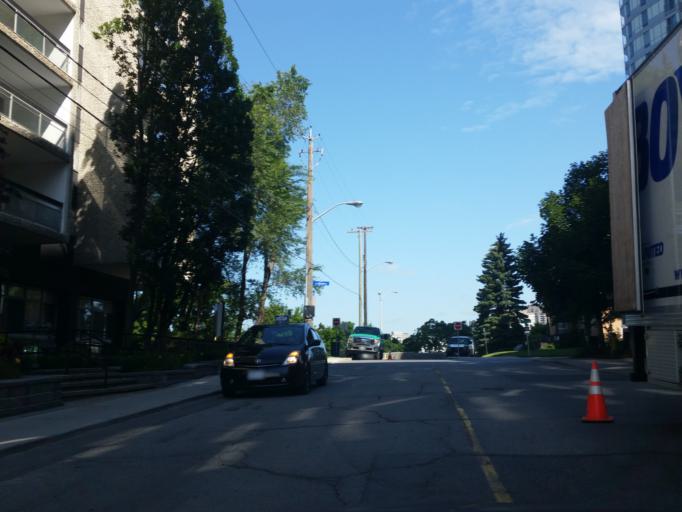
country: CA
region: Ontario
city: Ottawa
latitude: 45.4167
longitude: -75.7088
